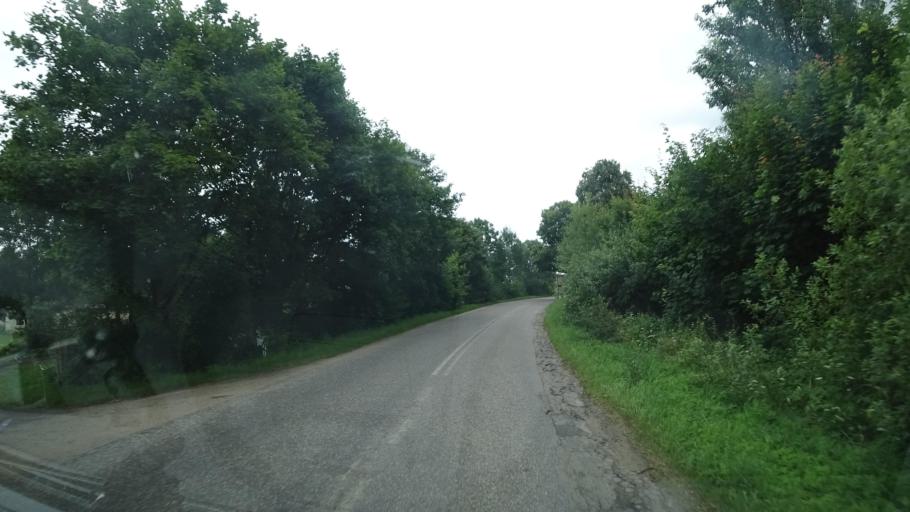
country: PL
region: Podlasie
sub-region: Powiat suwalski
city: Filipow
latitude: 54.2888
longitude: 22.5137
